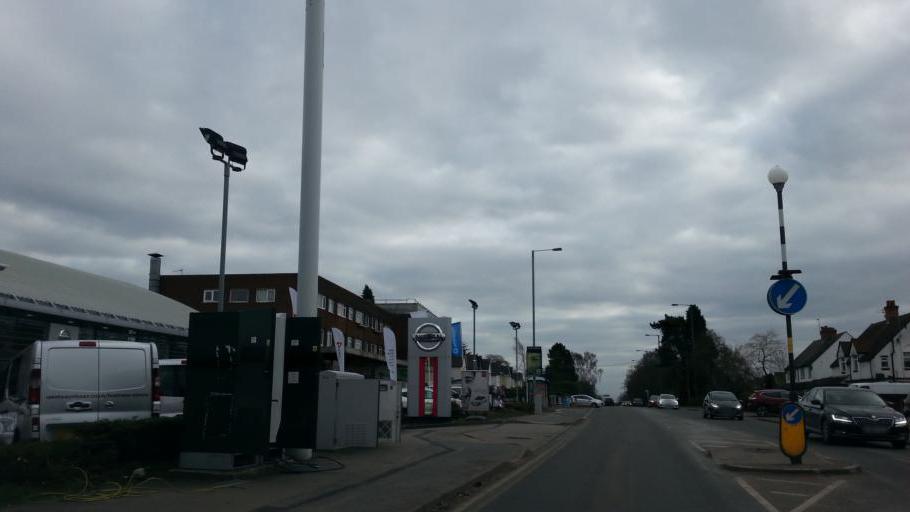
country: GB
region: England
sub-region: Walsall
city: Streetly
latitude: 52.5774
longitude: -1.8842
